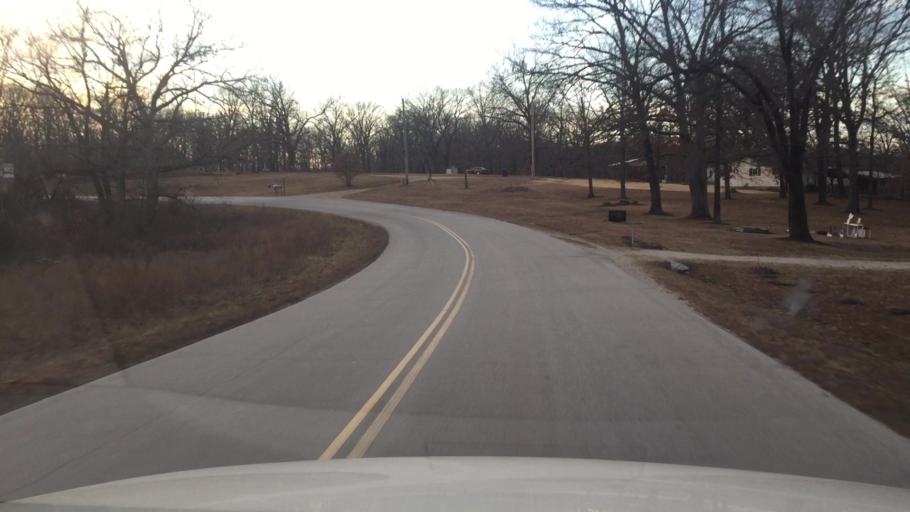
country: US
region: Missouri
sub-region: Morgan County
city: Versailles
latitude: 38.3359
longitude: -92.7661
